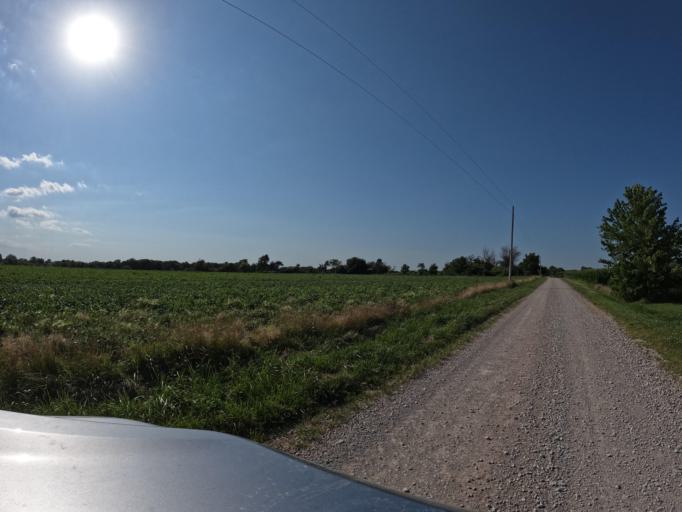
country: US
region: Iowa
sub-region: Appanoose County
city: Centerville
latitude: 40.7237
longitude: -93.0158
